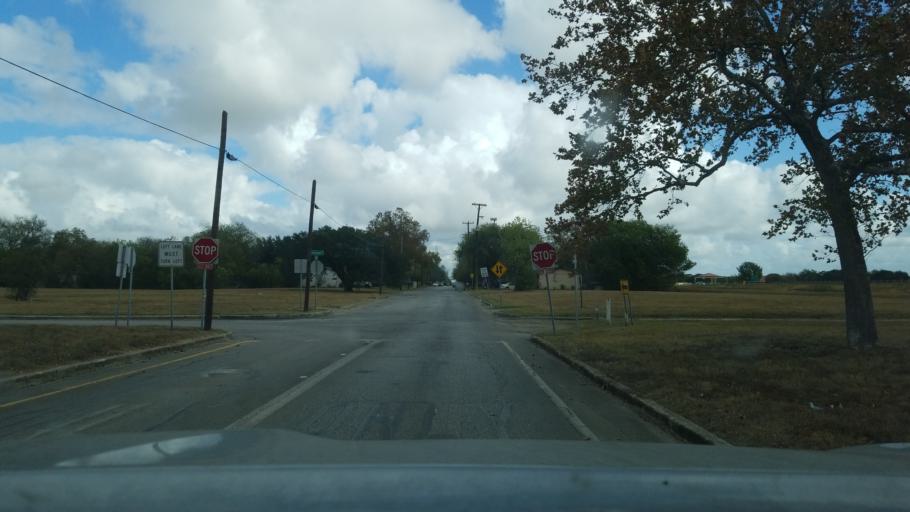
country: US
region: Texas
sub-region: Bexar County
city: Universal City
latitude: 29.5416
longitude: -98.2952
